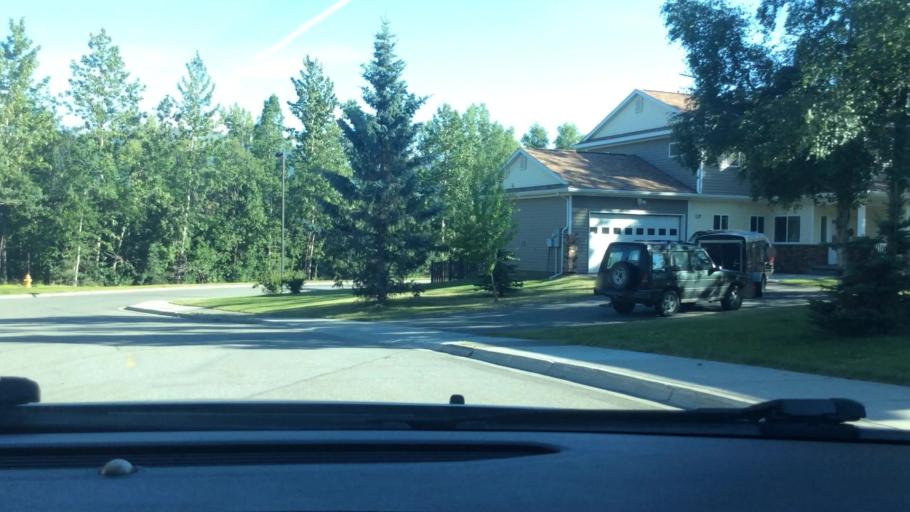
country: US
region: Alaska
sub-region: Anchorage Municipality
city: Elmendorf Air Force Base
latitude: 61.2518
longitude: -149.7008
